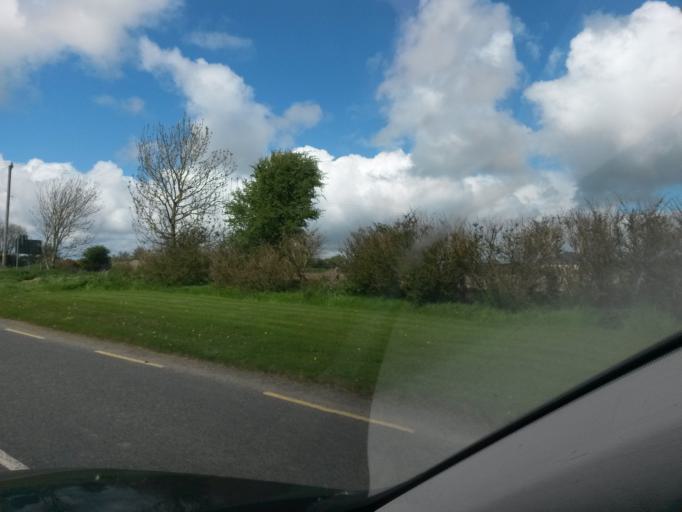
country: IE
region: Munster
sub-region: Waterford
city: Dunmore East
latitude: 52.2469
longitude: -6.8604
